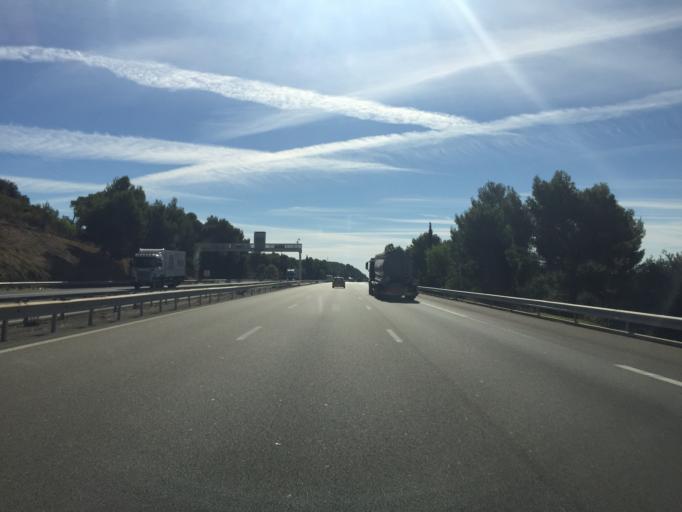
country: FR
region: Provence-Alpes-Cote d'Azur
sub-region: Departement des Bouches-du-Rhone
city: Salon-de-Provence
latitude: 43.6509
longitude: 5.1088
